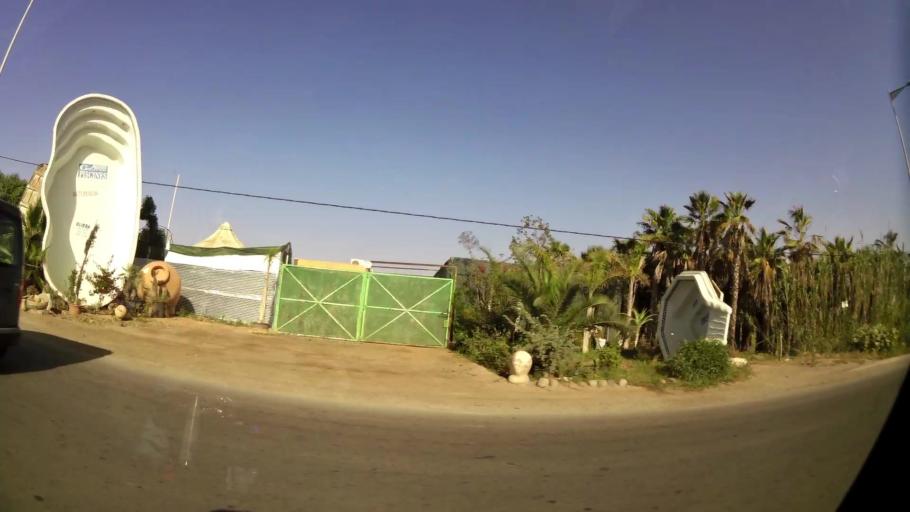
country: MA
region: Souss-Massa-Draa
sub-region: Inezgane-Ait Mellou
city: Inezgane
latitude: 30.3662
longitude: -9.5060
